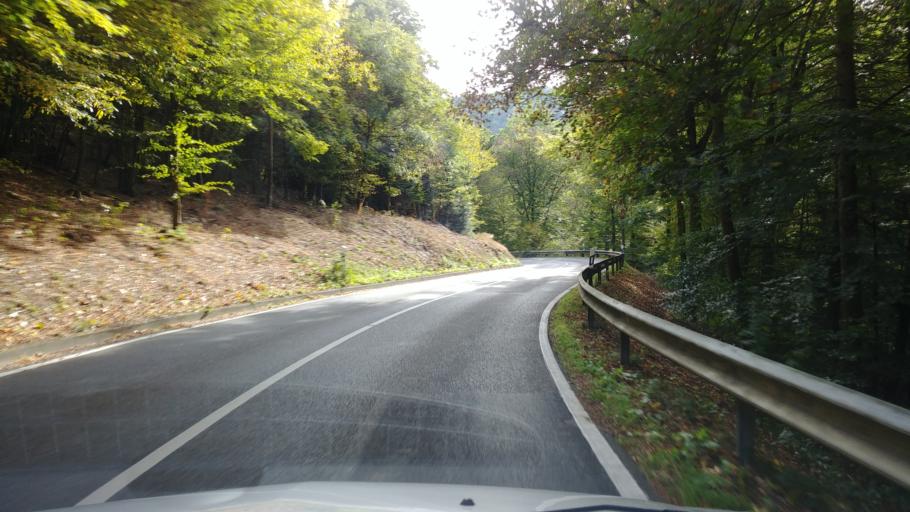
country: DE
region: Rheinland-Pfalz
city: Reckenroth
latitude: 50.2245
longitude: 8.0346
